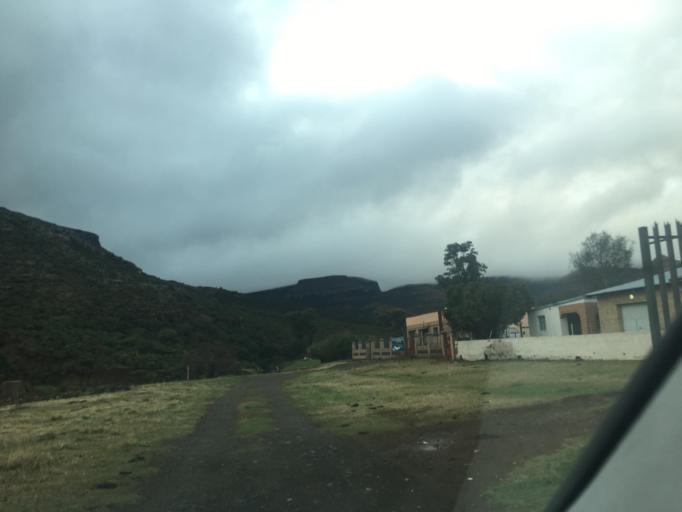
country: ZA
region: Eastern Cape
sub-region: Chris Hani District Municipality
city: Cala
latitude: -31.5225
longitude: 27.7039
